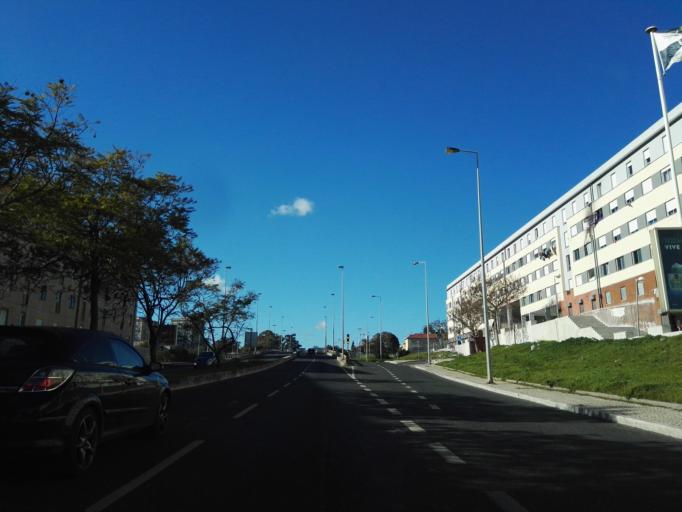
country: PT
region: Lisbon
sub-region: Loures
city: Sacavem
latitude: 38.7801
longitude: -9.1175
